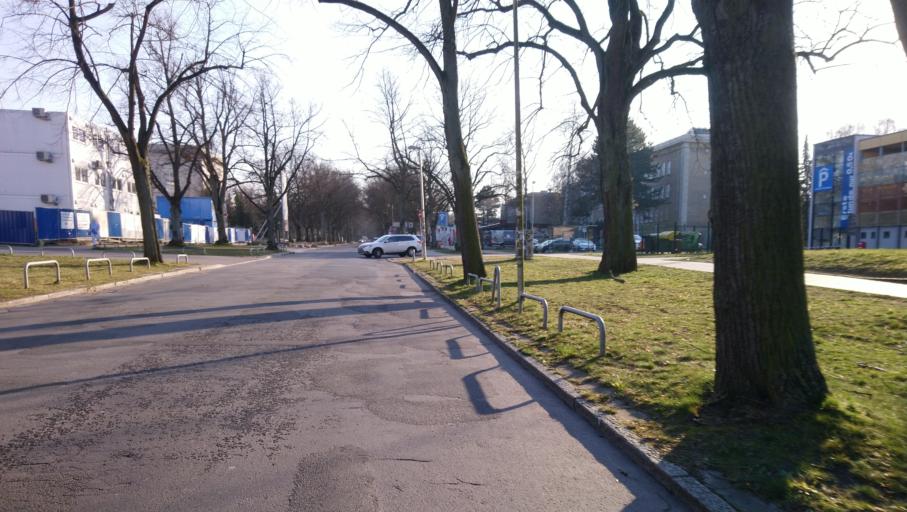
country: DE
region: Mecklenburg-Vorpommern
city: Rostock
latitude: 54.0860
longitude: 12.1010
